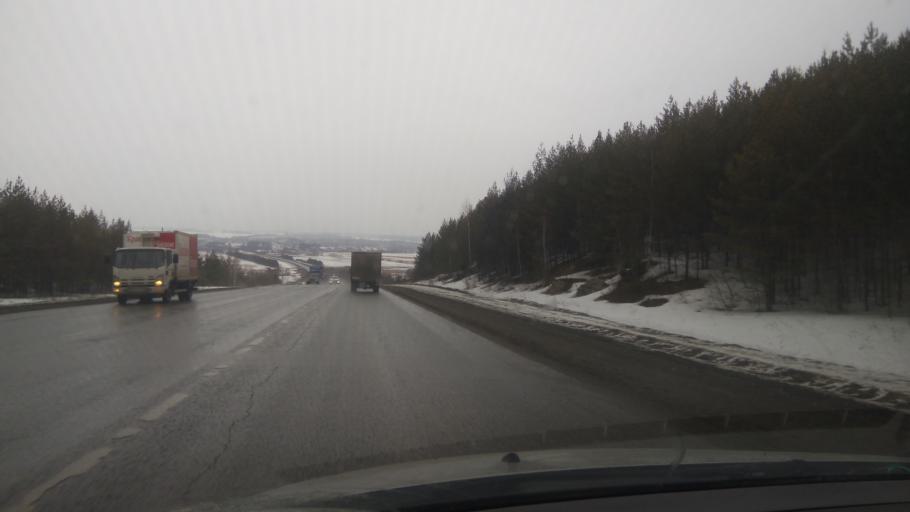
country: RU
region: Perm
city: Kungur
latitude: 57.3534
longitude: 56.9349
